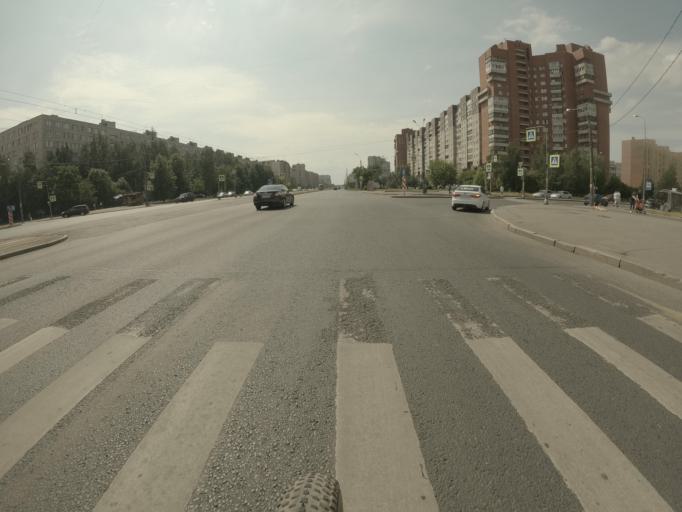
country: RU
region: St.-Petersburg
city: Krasnogvargeisky
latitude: 59.9220
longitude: 30.4793
